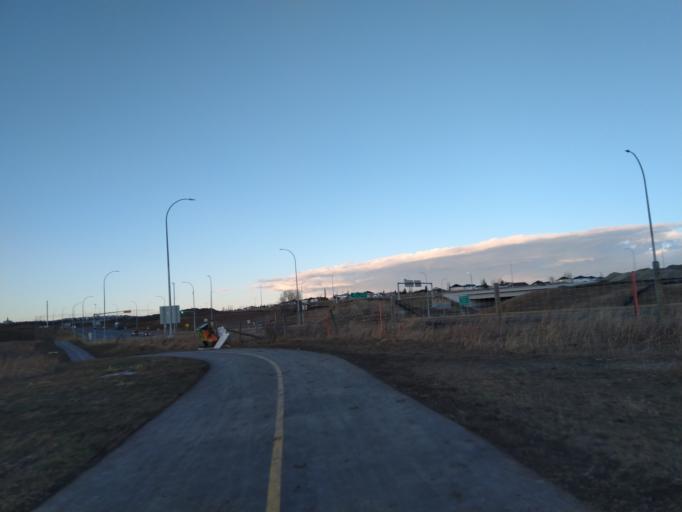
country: CA
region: Alberta
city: Calgary
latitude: 51.1172
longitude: -114.2336
